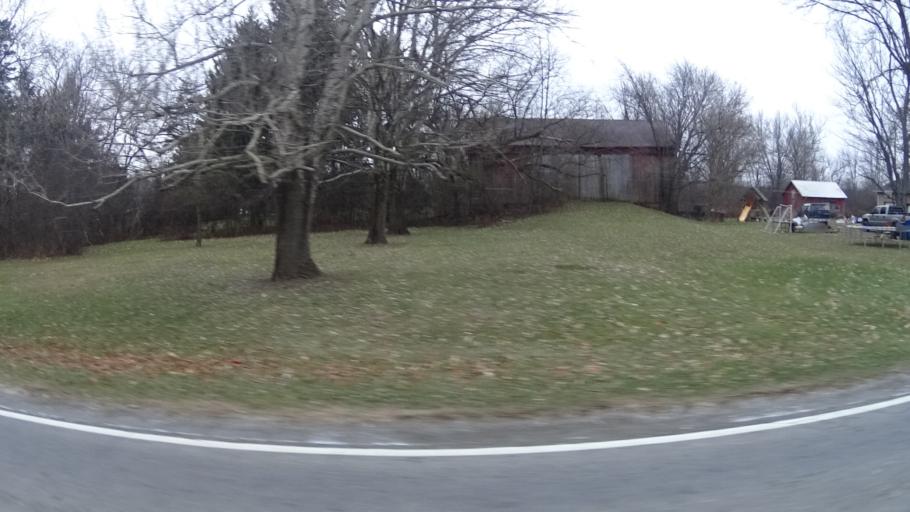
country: US
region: Ohio
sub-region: Lorain County
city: Oberlin
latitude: 41.3163
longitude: -82.2422
